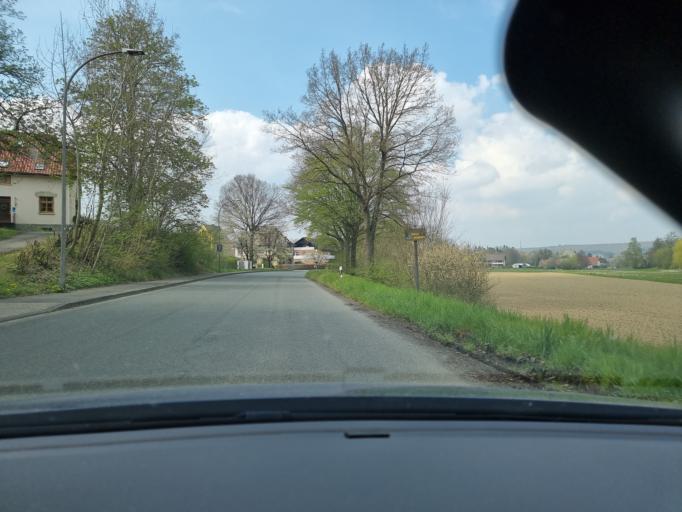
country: DE
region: North Rhine-Westphalia
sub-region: Regierungsbezirk Detmold
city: Dorentrup
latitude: 52.1390
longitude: 8.9640
